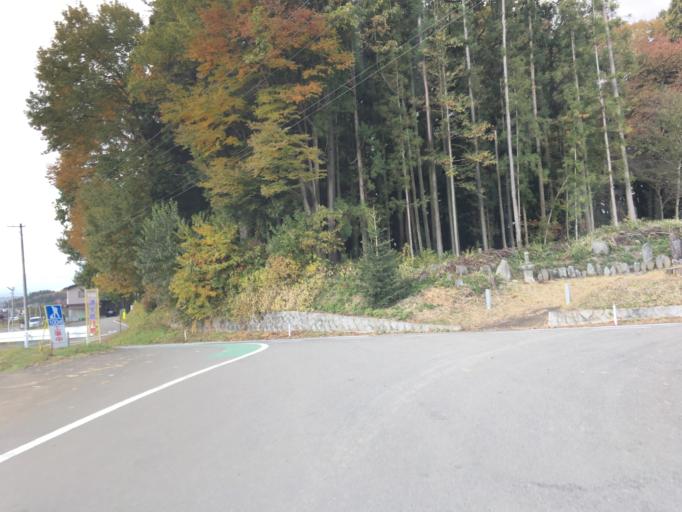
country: JP
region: Fukushima
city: Nihommatsu
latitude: 37.6308
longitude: 140.4685
